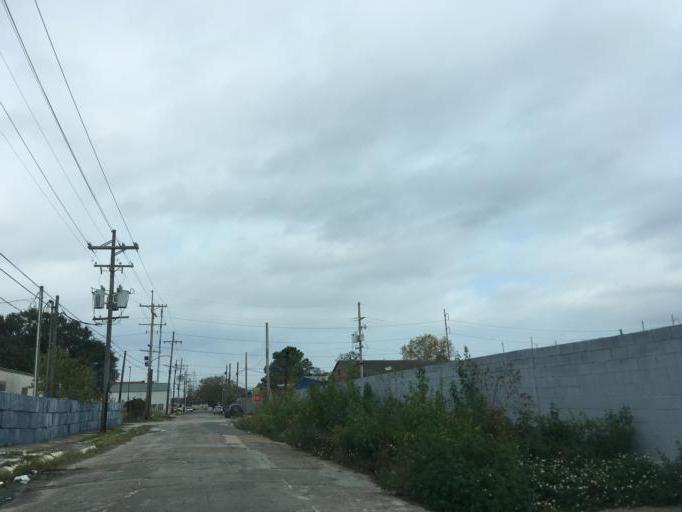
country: US
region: Louisiana
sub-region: Orleans Parish
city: New Orleans
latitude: 29.9871
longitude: -90.0596
